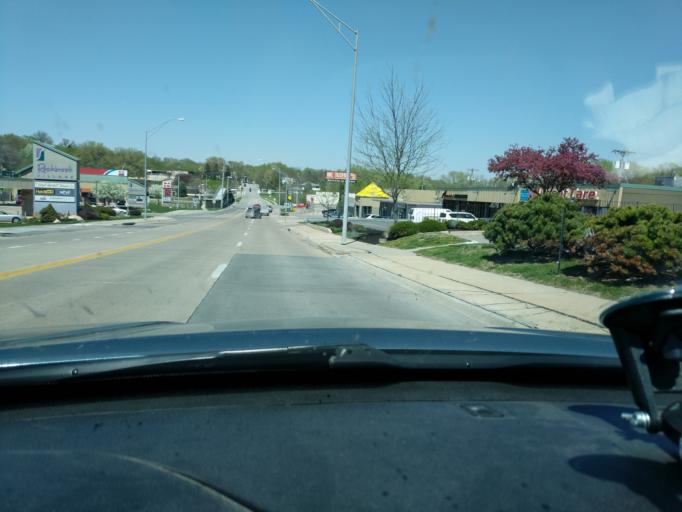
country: US
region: Nebraska
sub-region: Douglas County
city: Ralston
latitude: 41.2325
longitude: -96.0814
